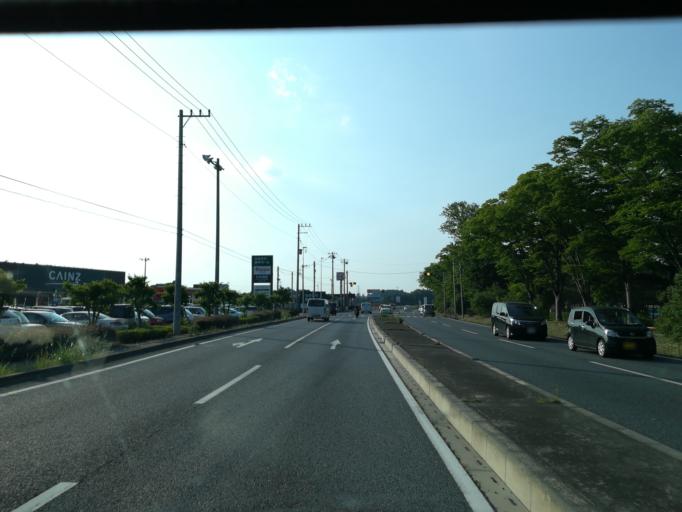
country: JP
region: Saitama
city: Kumagaya
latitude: 36.0599
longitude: 139.3698
